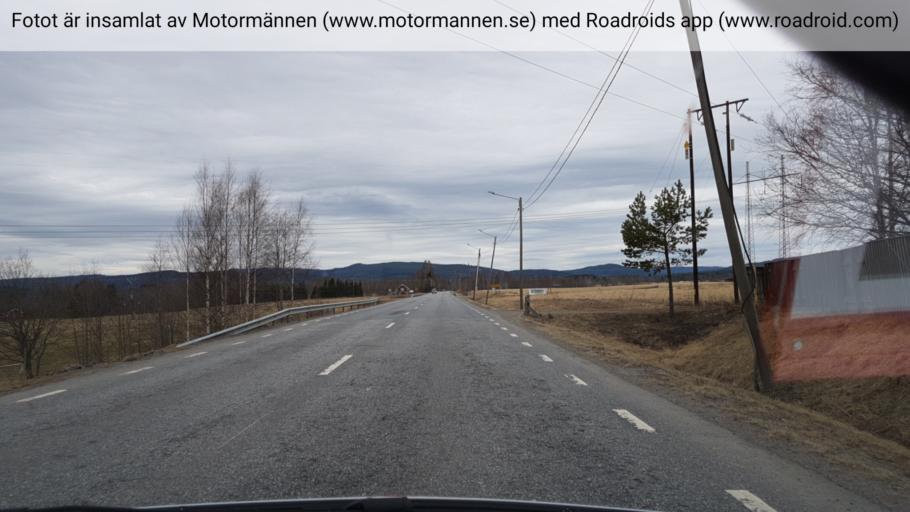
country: SE
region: Vaesternorrland
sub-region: Solleftea Kommun
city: Solleftea
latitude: 63.2321
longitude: 17.2136
